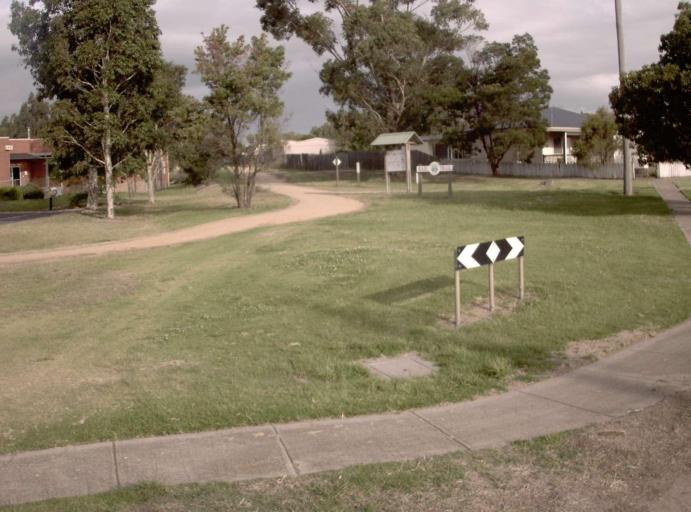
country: AU
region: Victoria
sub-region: Wellington
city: Sale
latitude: -37.9723
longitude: 146.9843
